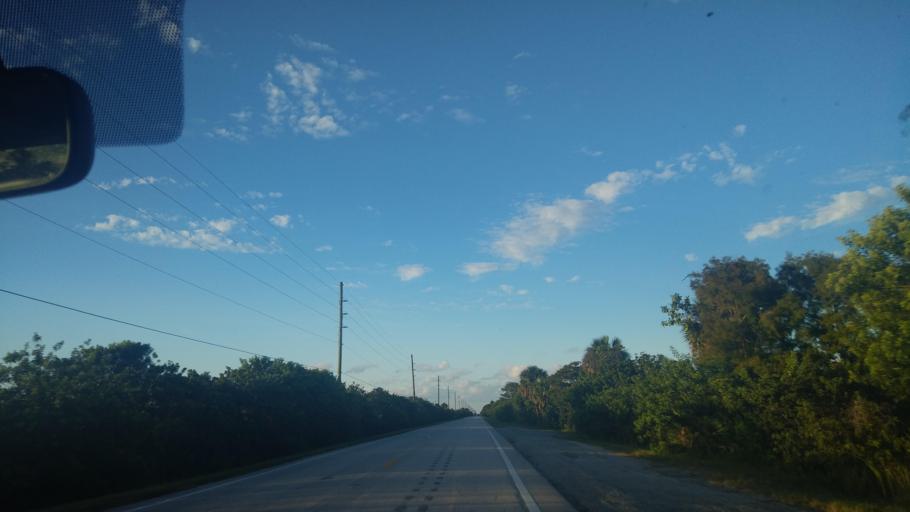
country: US
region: Florida
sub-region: Indian River County
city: Fellsmere
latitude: 27.6716
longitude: -80.6431
